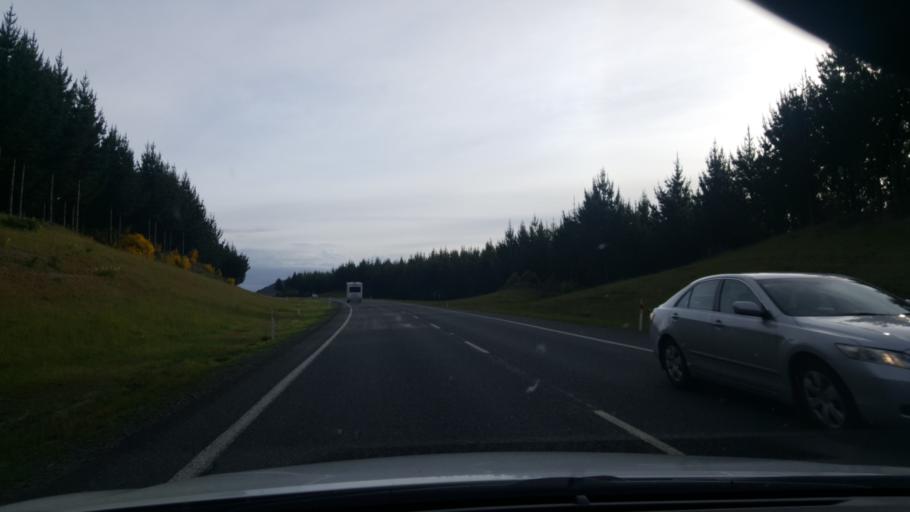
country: NZ
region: Waikato
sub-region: Taupo District
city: Taupo
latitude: -38.8253
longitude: 176.0691
